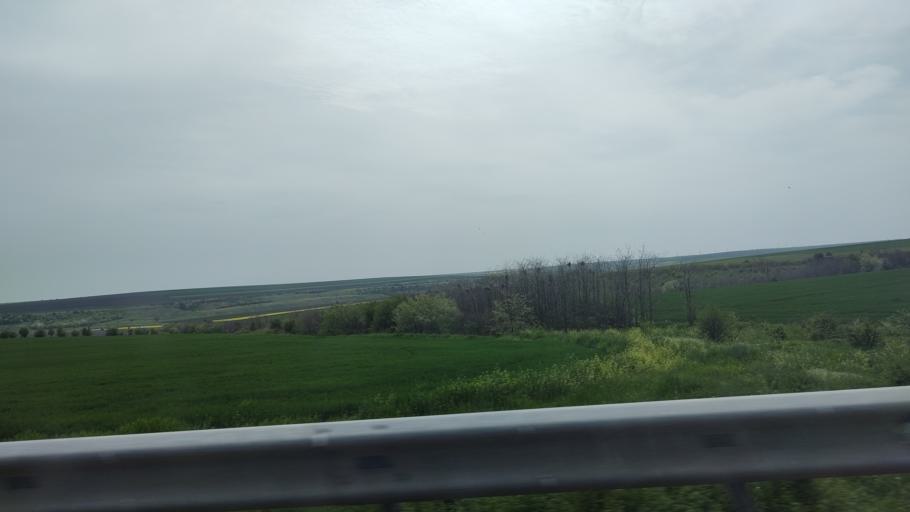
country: RO
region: Constanta
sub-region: Oras Murfatlar
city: Siminoc
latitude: 44.1413
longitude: 28.3552
